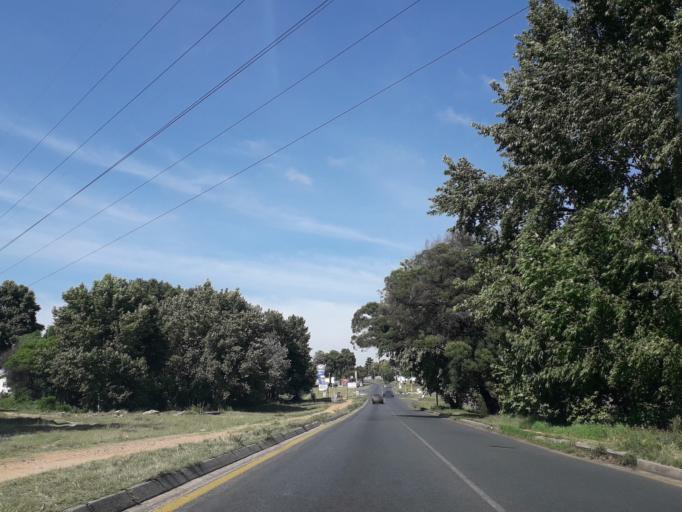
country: ZA
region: Gauteng
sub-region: City of Johannesburg Metropolitan Municipality
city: Roodepoort
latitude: -26.0711
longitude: 27.9662
